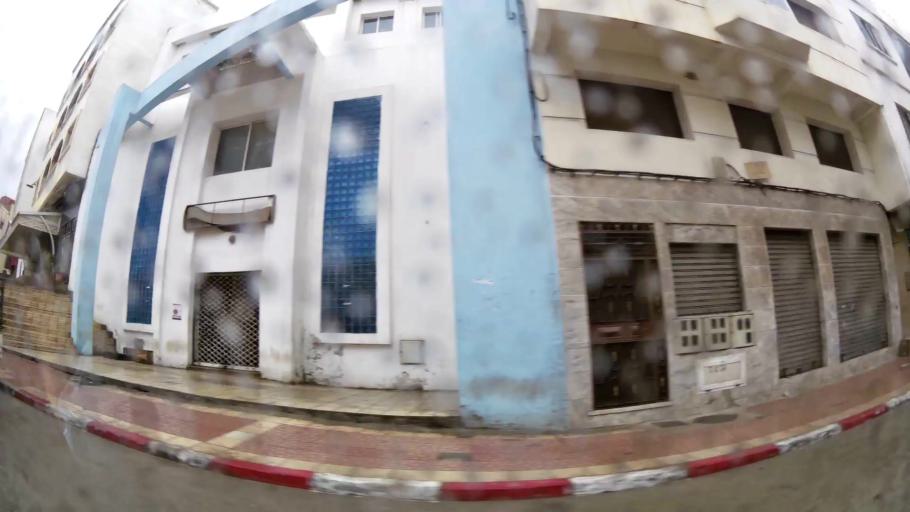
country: MA
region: Taza-Al Hoceima-Taounate
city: Al Hoceima
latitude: 35.2492
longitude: -3.9354
